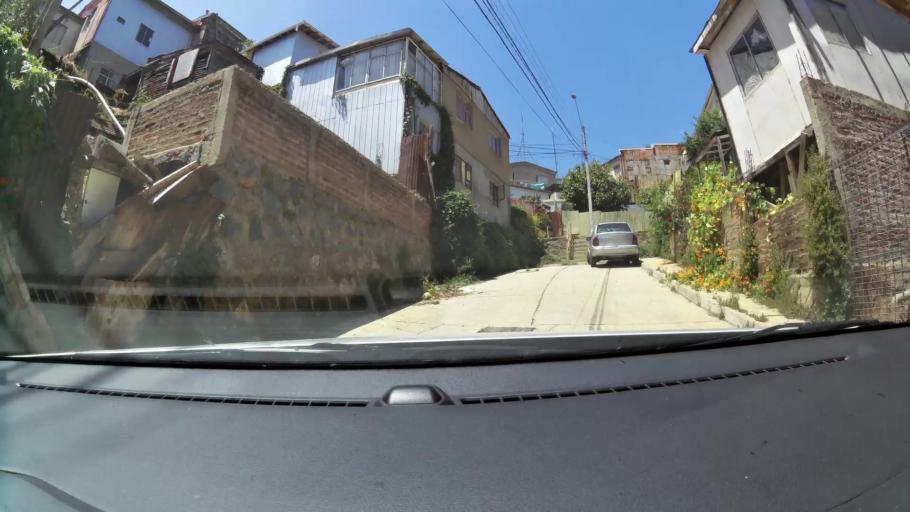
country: CL
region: Valparaiso
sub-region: Provincia de Valparaiso
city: Valparaiso
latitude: -33.0309
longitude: -71.6429
